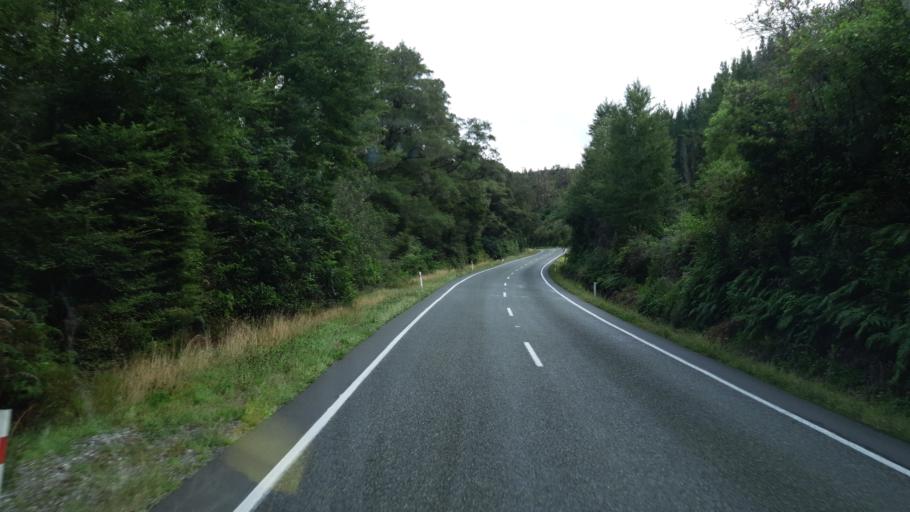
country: NZ
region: West Coast
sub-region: Buller District
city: Westport
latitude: -41.8255
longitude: 172.2384
